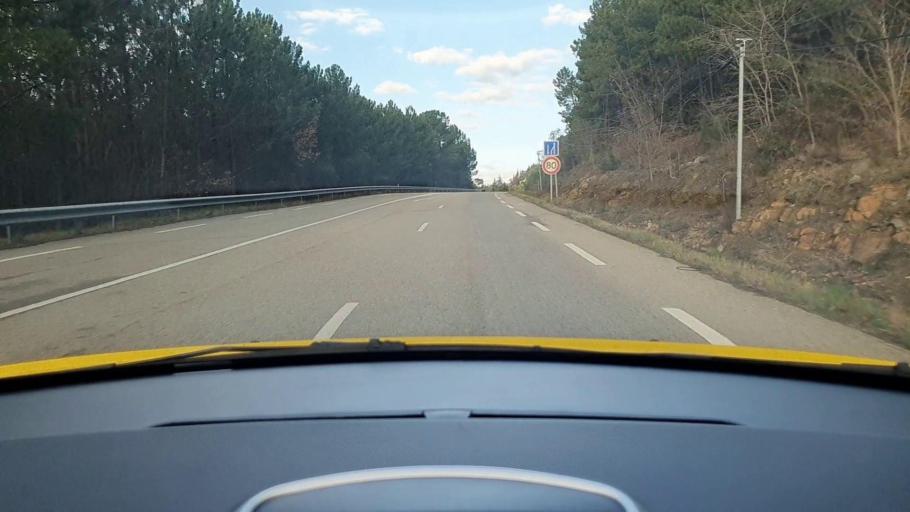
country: FR
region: Languedoc-Roussillon
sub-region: Departement du Gard
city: Les Salles-du-Gardon
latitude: 44.2603
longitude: 4.0371
